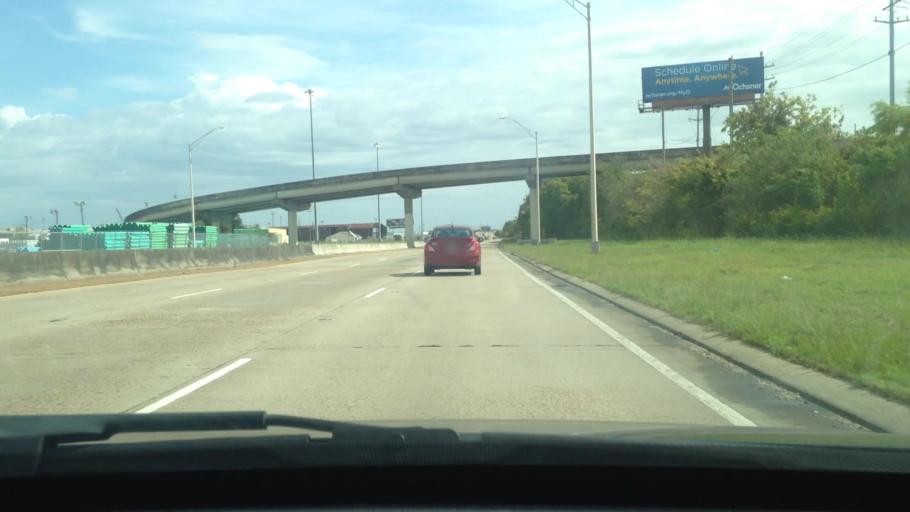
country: US
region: Louisiana
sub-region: Jefferson Parish
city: Jefferson
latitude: 29.9699
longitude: -90.1468
